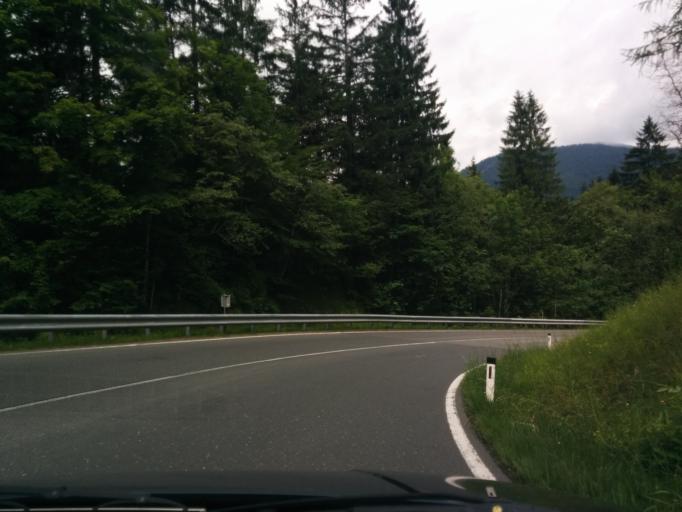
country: AT
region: Salzburg
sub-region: Politischer Bezirk Hallein
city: Abtenau
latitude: 47.5860
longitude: 13.3178
